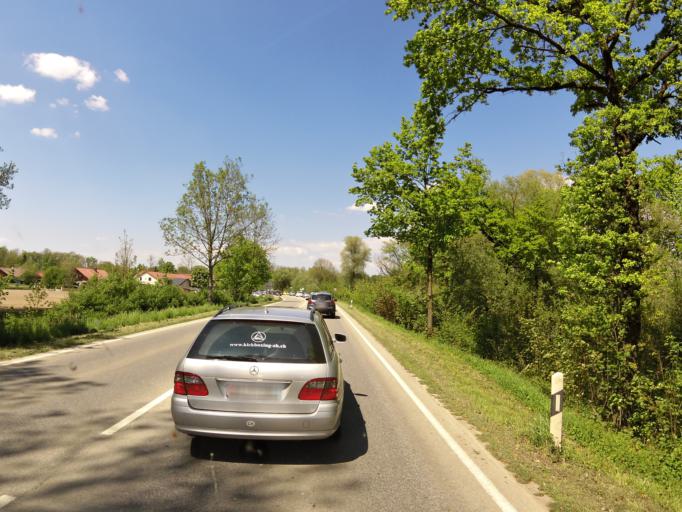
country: DE
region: Bavaria
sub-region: Lower Bavaria
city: Plattling
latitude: 48.7679
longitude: 12.8900
